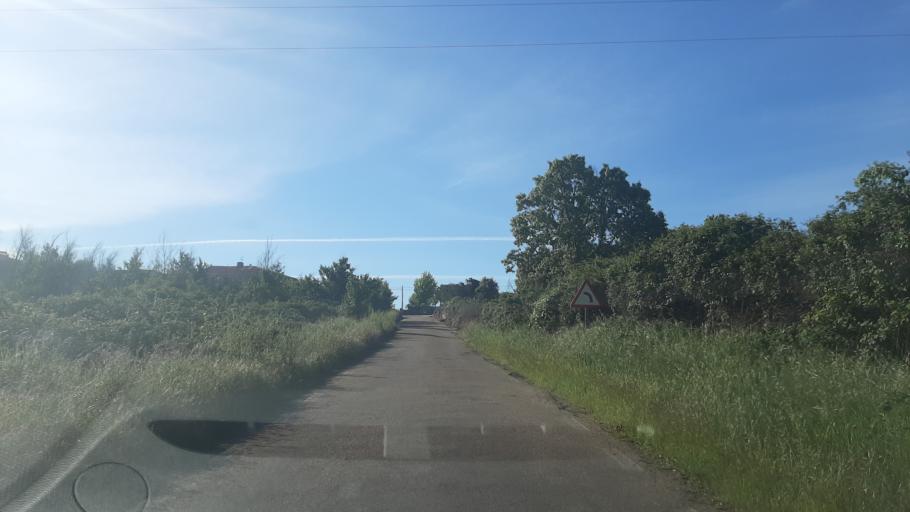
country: ES
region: Castille and Leon
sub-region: Provincia de Salamanca
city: Guijo de Avila
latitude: 40.5306
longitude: -5.6439
